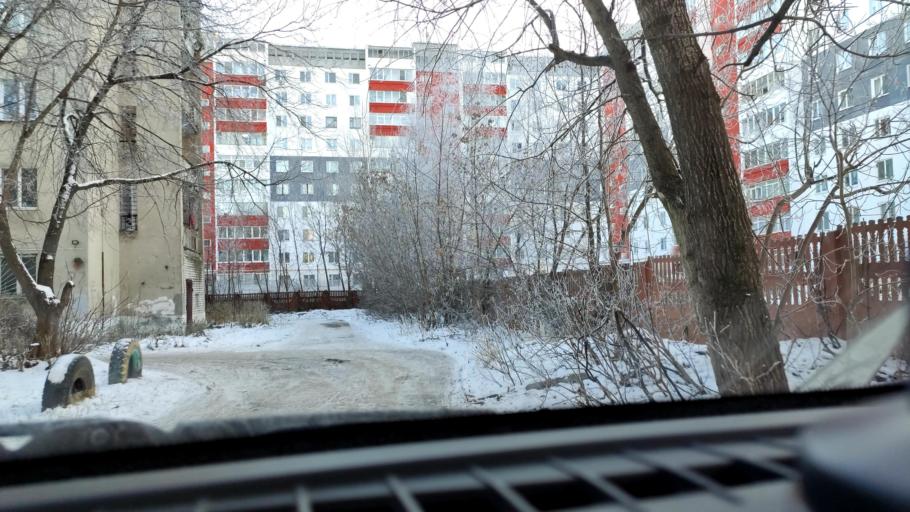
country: RU
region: Perm
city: Kondratovo
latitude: 58.0259
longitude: 56.0185
